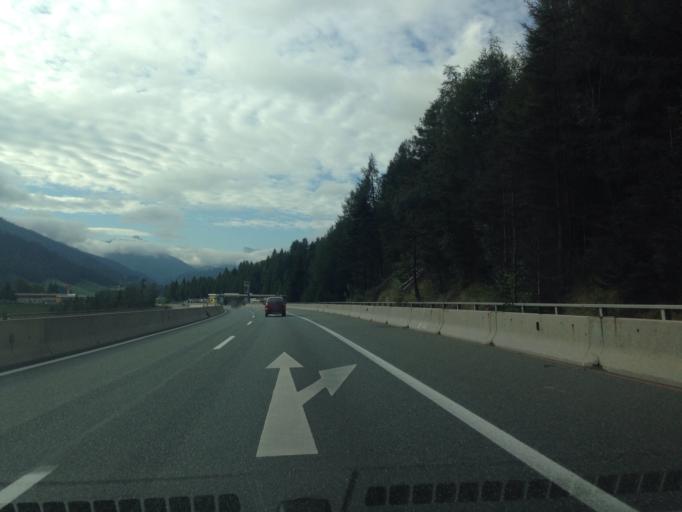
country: AT
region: Tyrol
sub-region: Politischer Bezirk Innsbruck Land
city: Matrei am Brenner
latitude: 47.1439
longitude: 11.4454
